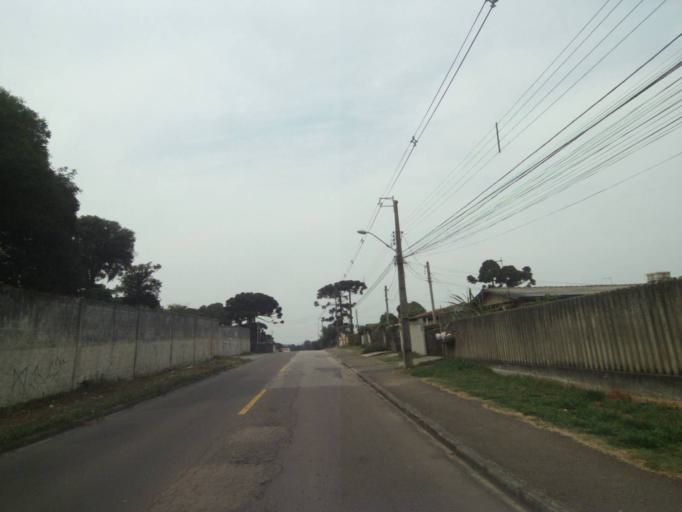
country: BR
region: Parana
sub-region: Sao Jose Dos Pinhais
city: Sao Jose dos Pinhais
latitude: -25.5285
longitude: -49.2824
